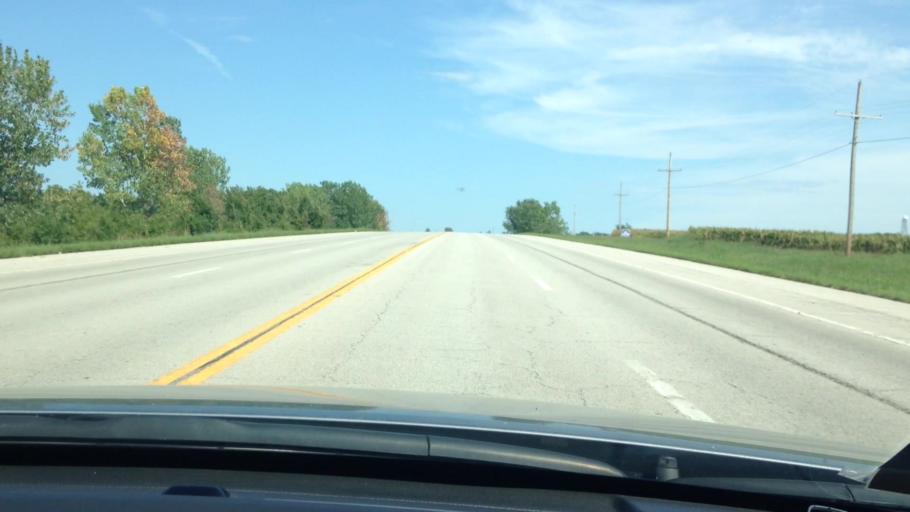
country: US
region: Missouri
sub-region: Cass County
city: Belton
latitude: 38.8175
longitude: -94.5807
